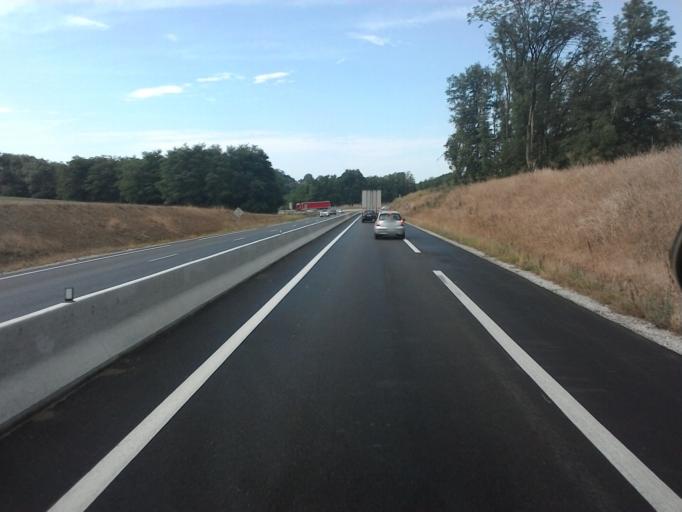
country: FR
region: Franche-Comte
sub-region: Departement du Jura
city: Lons-le-Saunier
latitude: 46.7094
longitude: 5.5506
